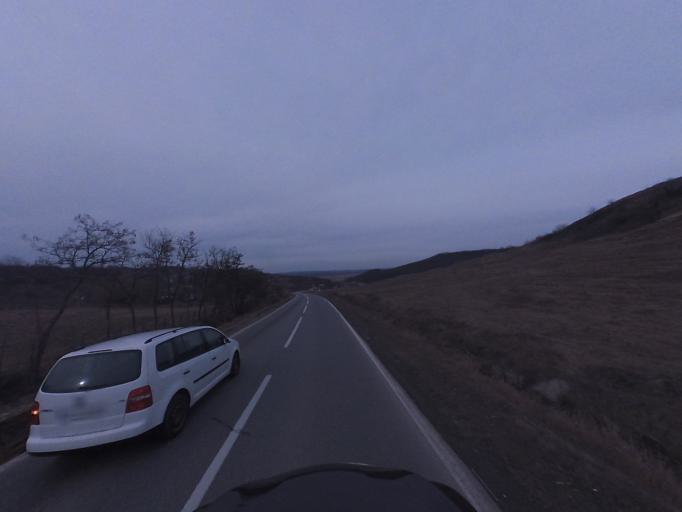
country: RO
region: Iasi
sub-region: Comuna Popricani
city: Popricani
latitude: 47.2930
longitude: 27.5109
